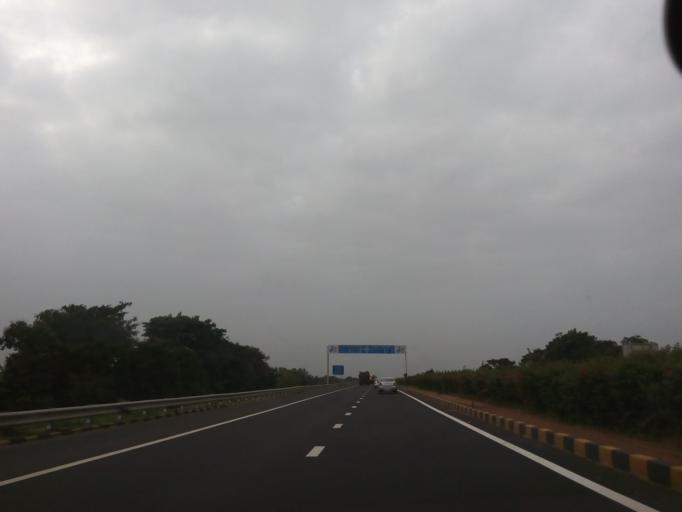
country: IN
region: Gujarat
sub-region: Kheda
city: Chaklasi
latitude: 22.6060
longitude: 72.9730
